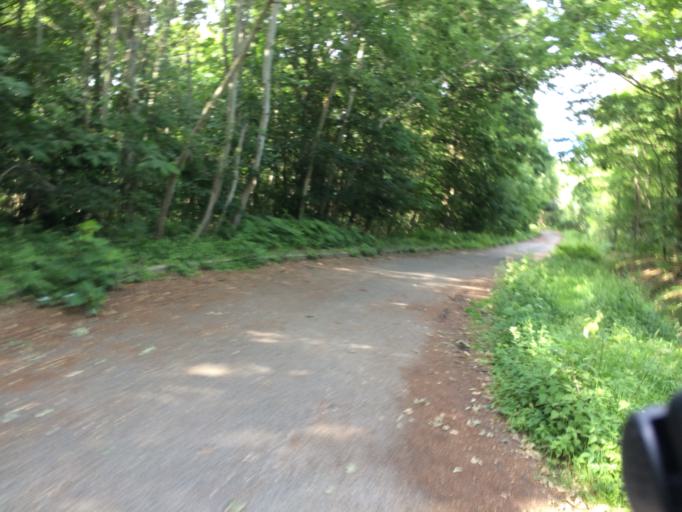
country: FR
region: Ile-de-France
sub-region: Departement de l'Essonne
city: Igny
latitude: 48.7520
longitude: 2.2347
